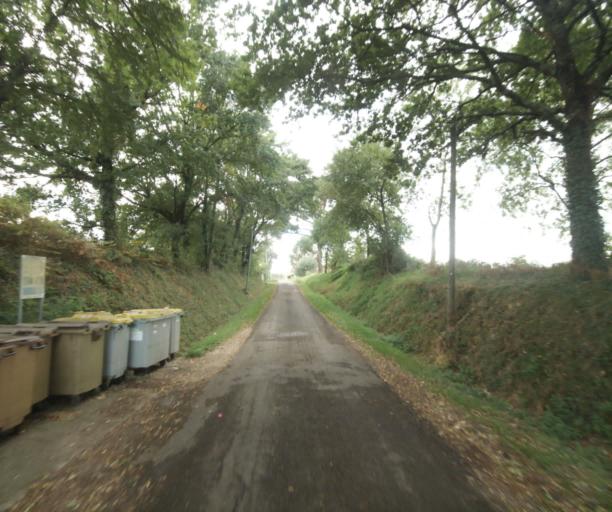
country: FR
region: Midi-Pyrenees
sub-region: Departement du Gers
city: Cazaubon
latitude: 43.8546
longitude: -0.1069
